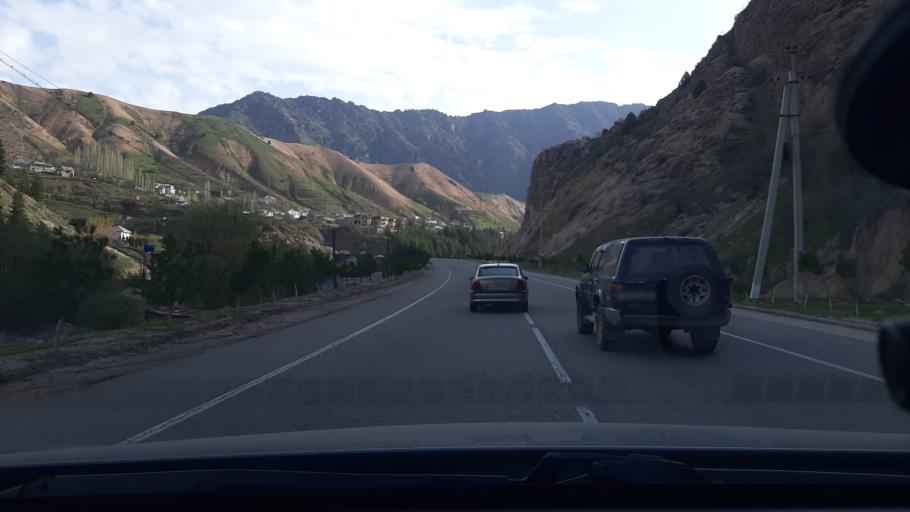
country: TJ
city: Tagob
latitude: 38.8418
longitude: 68.8333
